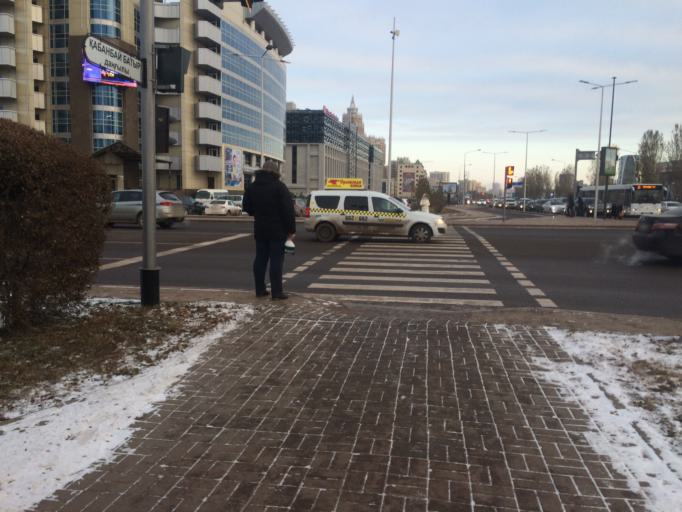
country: KZ
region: Astana Qalasy
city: Astana
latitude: 51.1331
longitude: 71.4140
